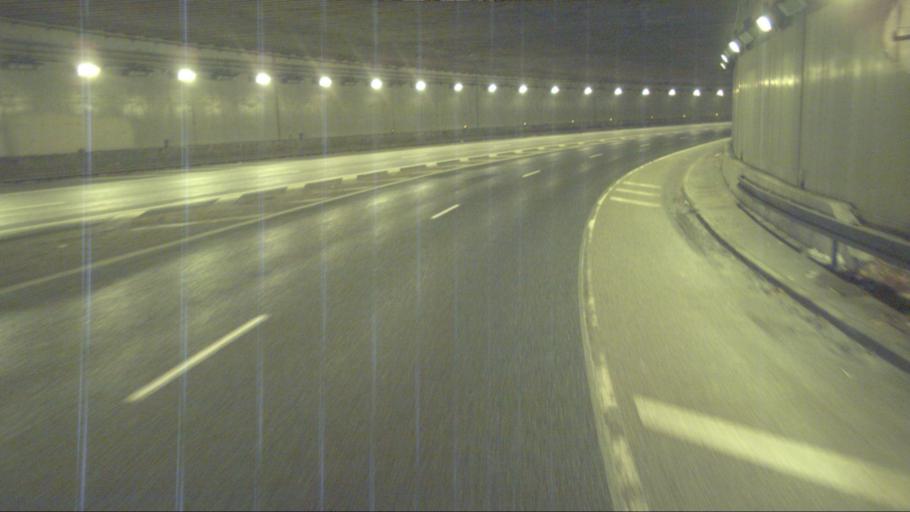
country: FR
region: Ile-de-France
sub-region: Departement des Yvelines
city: Chatou
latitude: 48.8725
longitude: 2.1572
